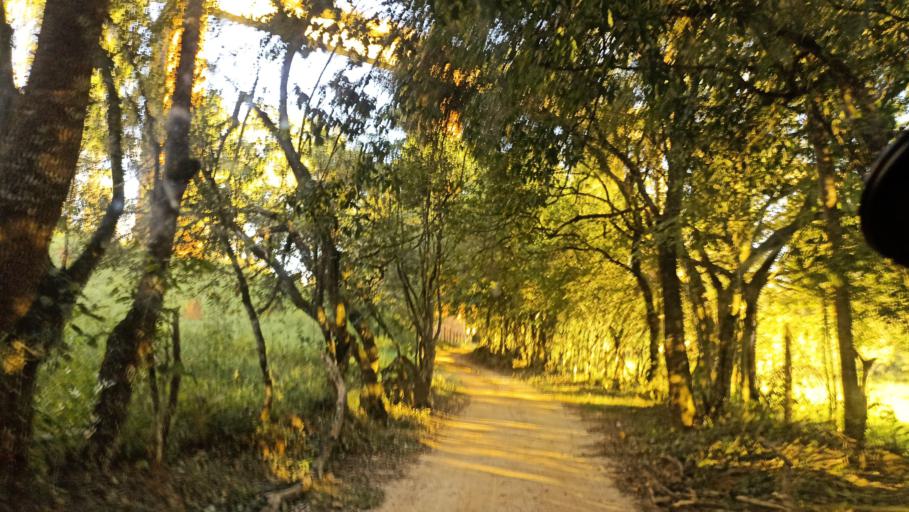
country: BR
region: Minas Gerais
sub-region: Sao Joao Del Rei
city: Sao Joao del Rei
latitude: -21.1808
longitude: -44.3546
